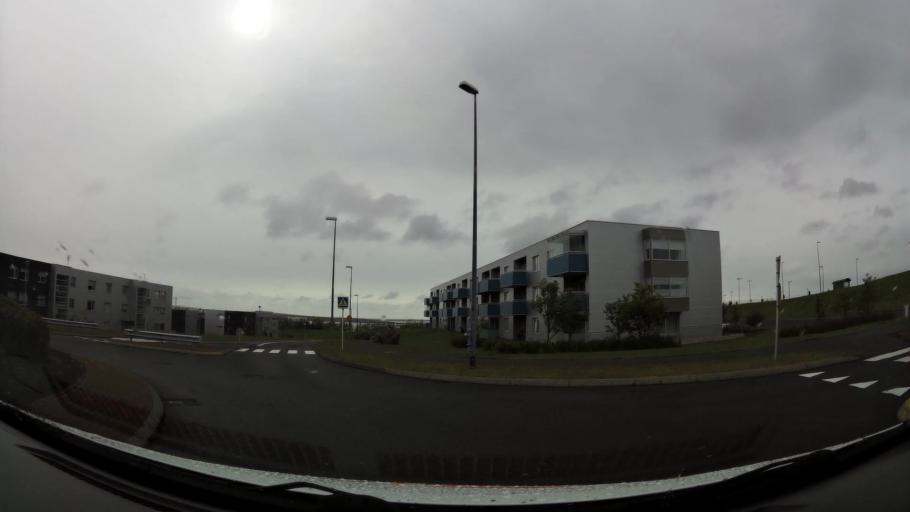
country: IS
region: Capital Region
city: Kopavogur
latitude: 64.0987
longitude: -21.9127
